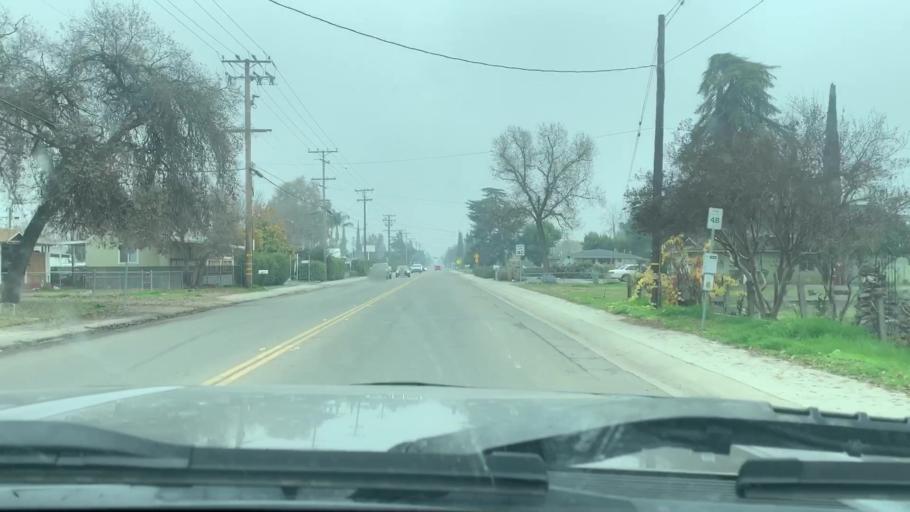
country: US
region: California
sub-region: Tulare County
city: Visalia
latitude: 36.3243
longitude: -119.3363
